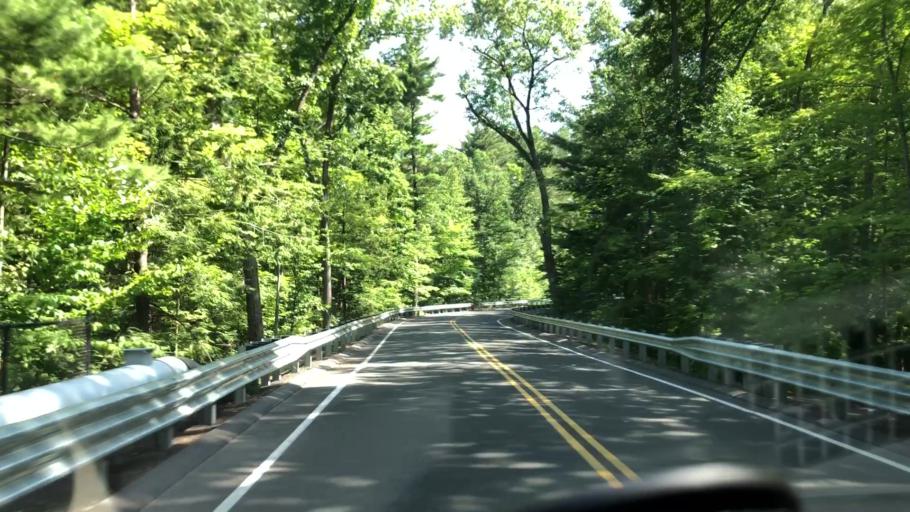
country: US
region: Massachusetts
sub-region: Hampden County
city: Holyoke
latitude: 42.1880
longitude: -72.6534
